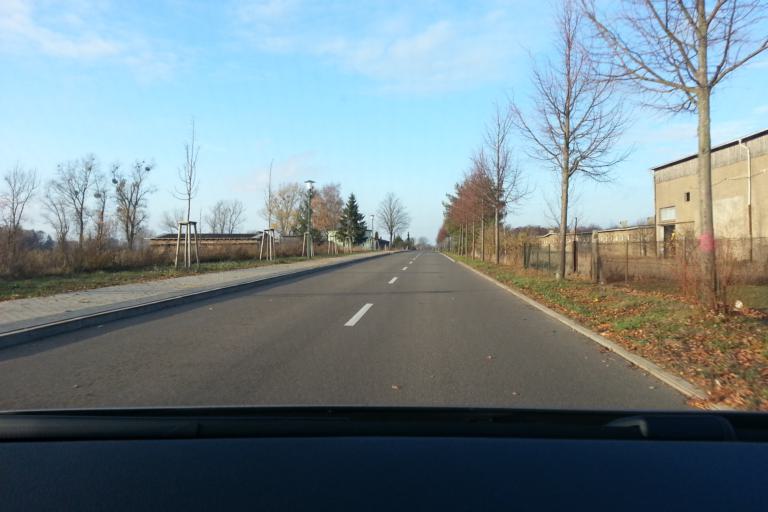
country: DE
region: Mecklenburg-Vorpommern
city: Strasburg
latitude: 53.6173
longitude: 13.7677
